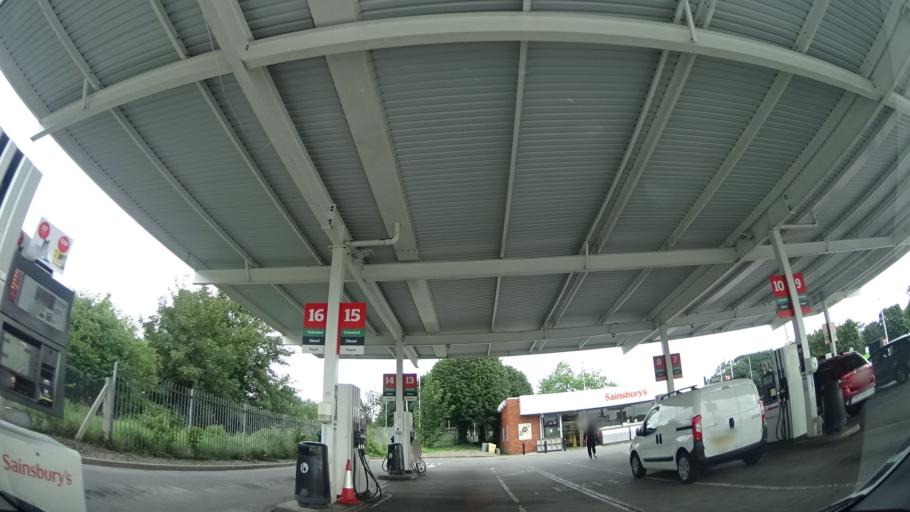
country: GB
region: England
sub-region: Knowsley
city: Knowsley
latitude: 53.4162
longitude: -2.9000
